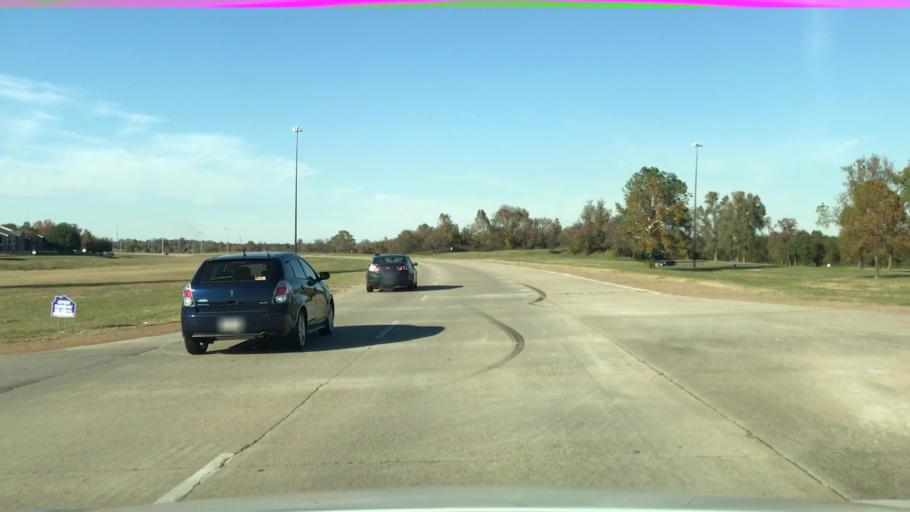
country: US
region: Louisiana
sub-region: Bossier Parish
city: Bossier City
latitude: 32.4691
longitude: -93.6857
